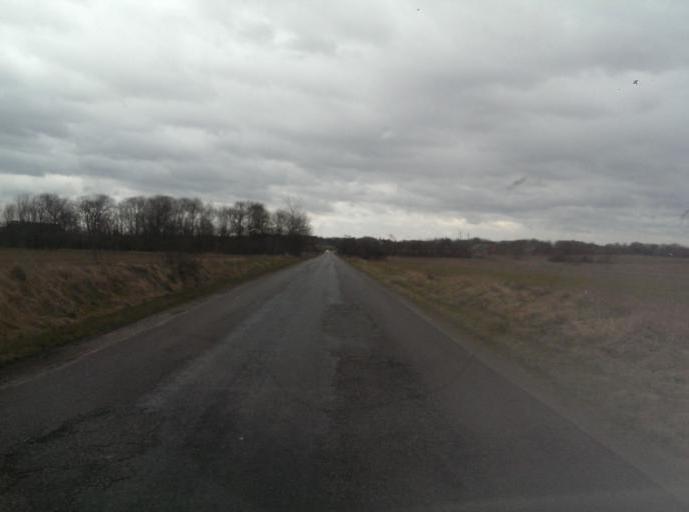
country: DK
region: Central Jutland
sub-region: Ringkobing-Skjern Kommune
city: Ringkobing
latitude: 56.1182
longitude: 8.4106
